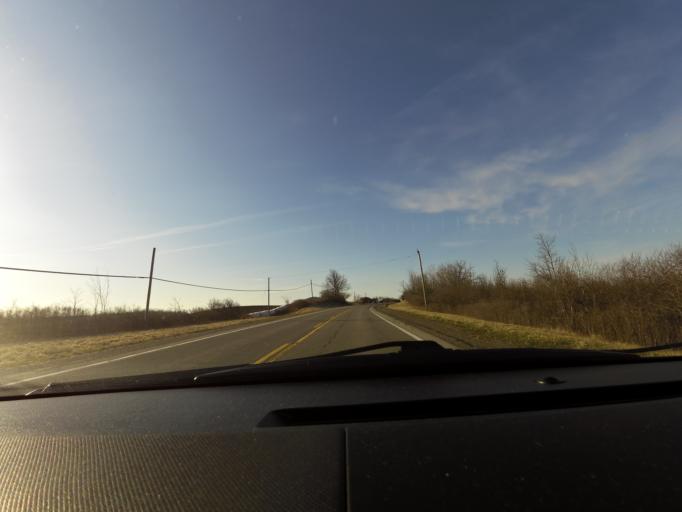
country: CA
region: Ontario
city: Ancaster
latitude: 42.9950
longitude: -79.8659
